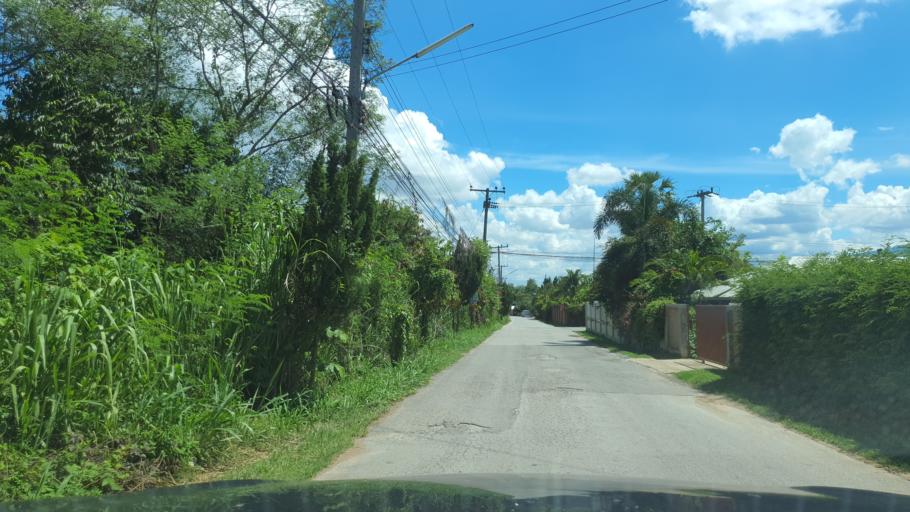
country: TH
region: Chiang Mai
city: San Sai
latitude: 18.9073
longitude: 99.0440
